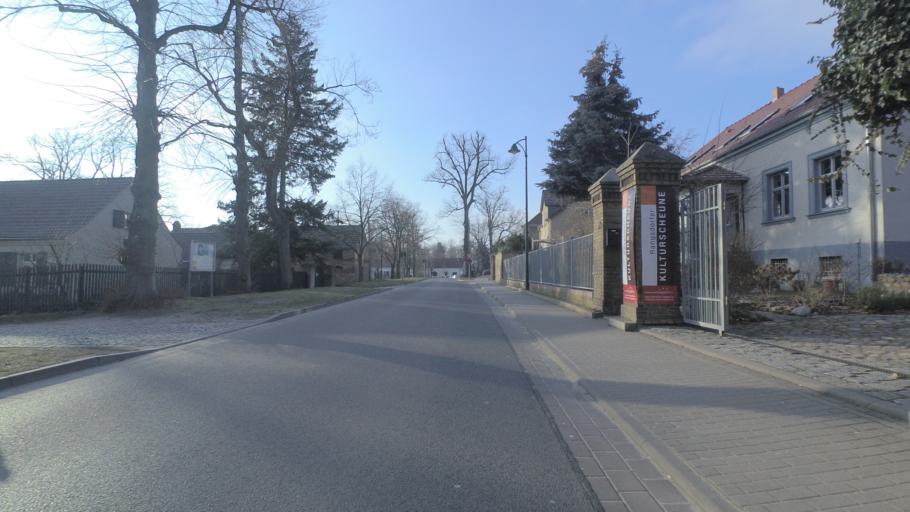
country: DE
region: Brandenburg
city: Rangsdorf
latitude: 52.2917
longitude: 13.4192
